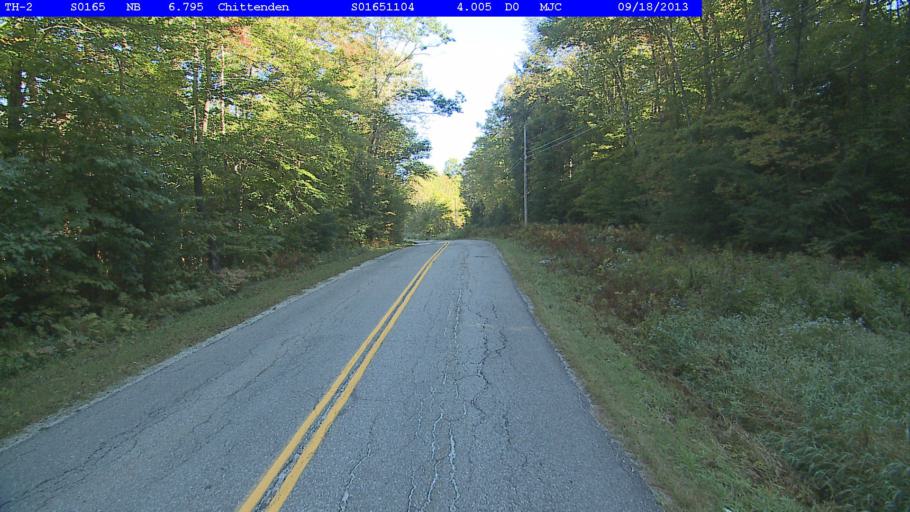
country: US
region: Vermont
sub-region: Rutland County
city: Rutland
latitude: 43.7318
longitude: -72.9709
